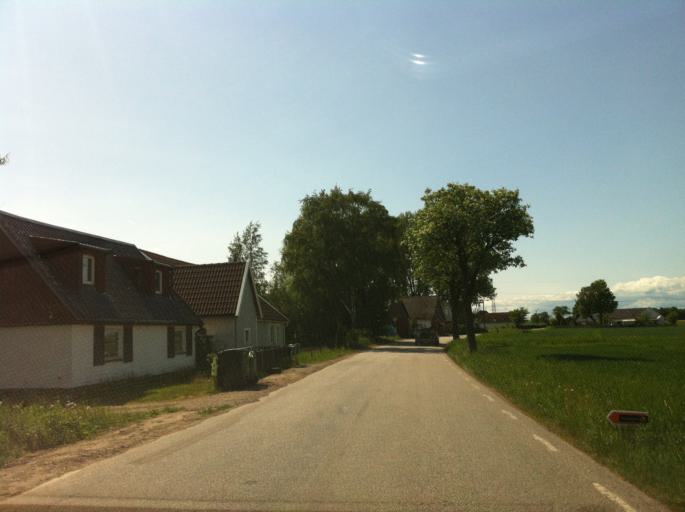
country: SE
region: Skane
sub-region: Landskrona
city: Asmundtorp
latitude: 55.9256
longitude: 12.9520
